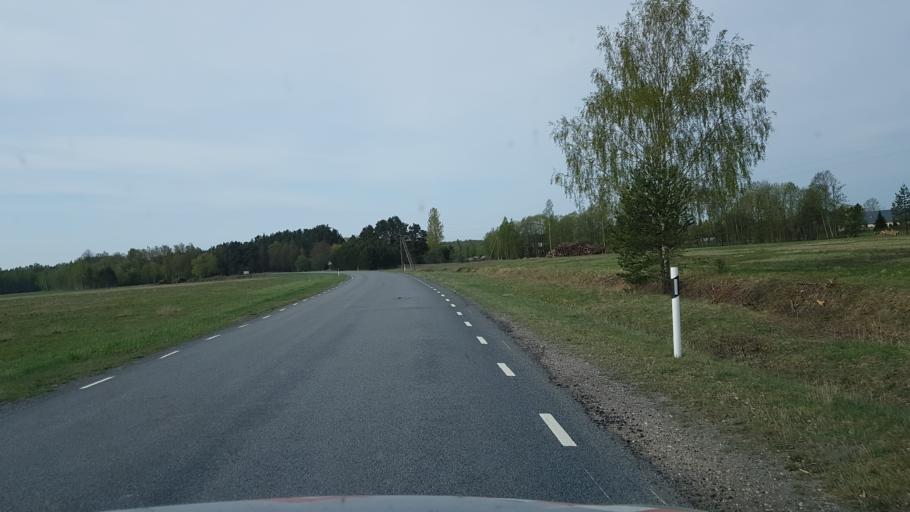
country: EE
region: Paernumaa
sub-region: Audru vald
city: Audru
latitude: 58.3602
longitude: 24.2591
